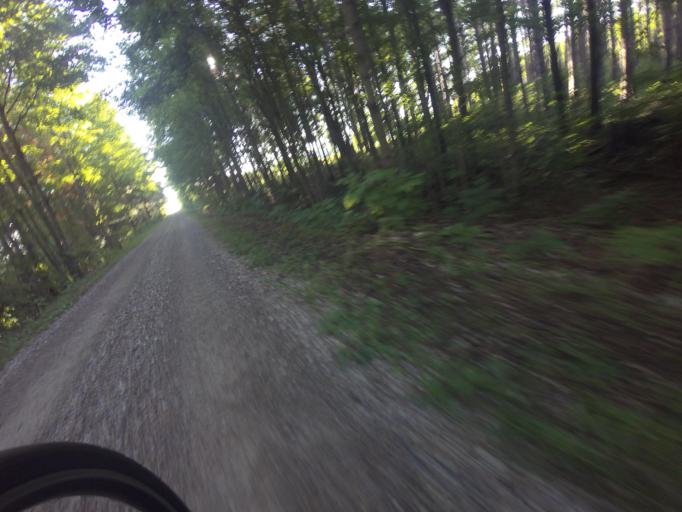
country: CA
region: Ontario
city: Goderich
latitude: 43.7539
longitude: -81.5638
